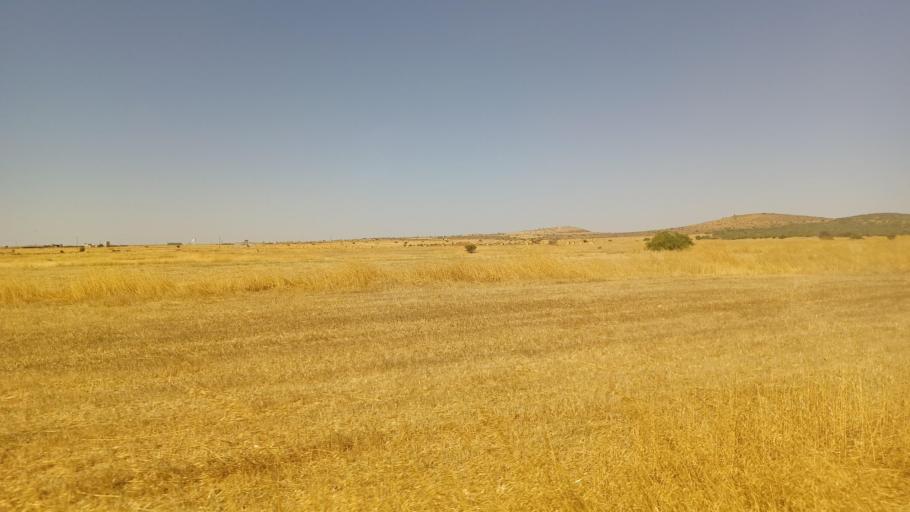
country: CY
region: Larnaka
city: Pergamos
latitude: 35.0417
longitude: 33.6847
